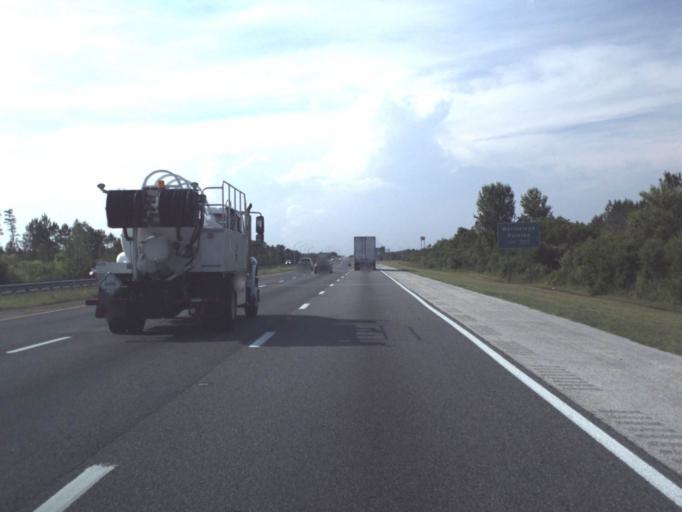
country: US
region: Florida
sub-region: Saint Johns County
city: Saint Augustine Shores
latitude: 29.7379
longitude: -81.3424
